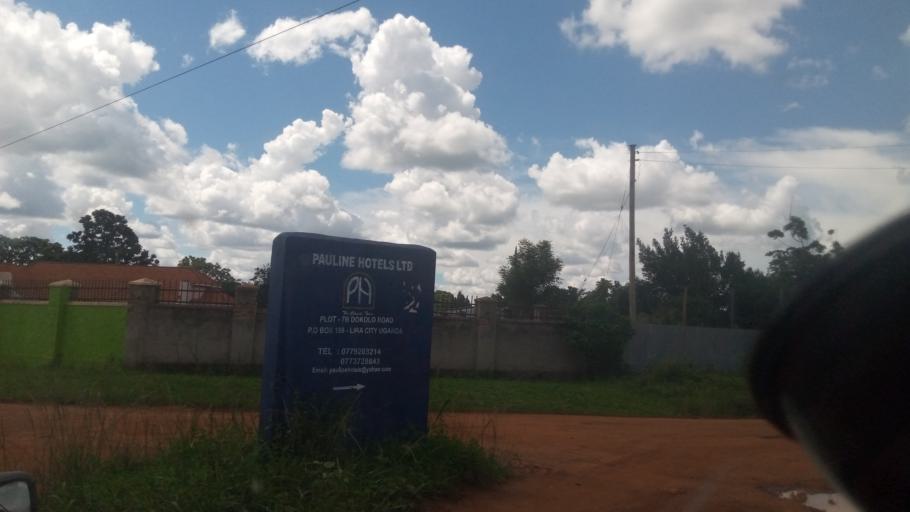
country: UG
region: Northern Region
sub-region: Lira District
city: Lira
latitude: 2.2404
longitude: 32.9038
